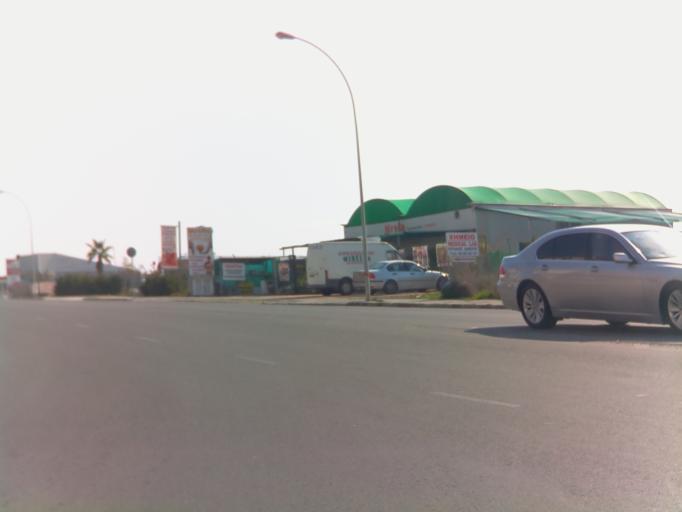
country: CY
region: Larnaka
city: Larnaca
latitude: 34.9117
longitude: 33.6113
